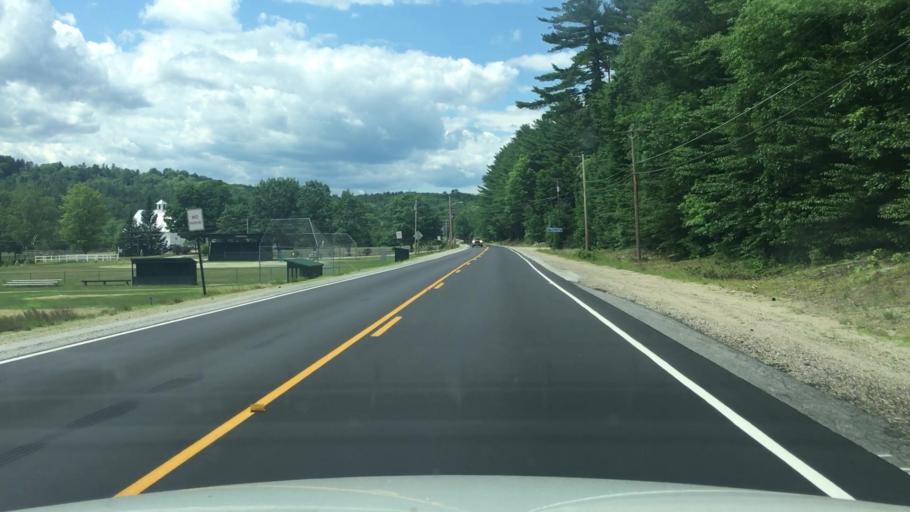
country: US
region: Maine
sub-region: Oxford County
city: West Paris
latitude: 44.3839
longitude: -70.6531
